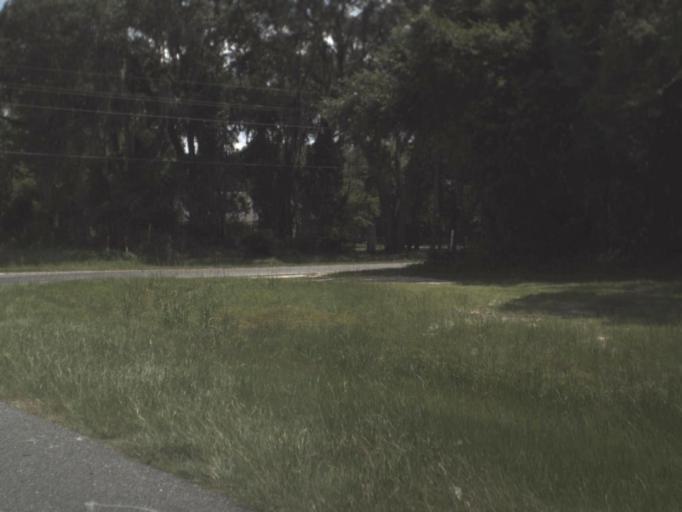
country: US
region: Florida
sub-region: Columbia County
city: Watertown
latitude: 30.0294
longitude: -82.5977
